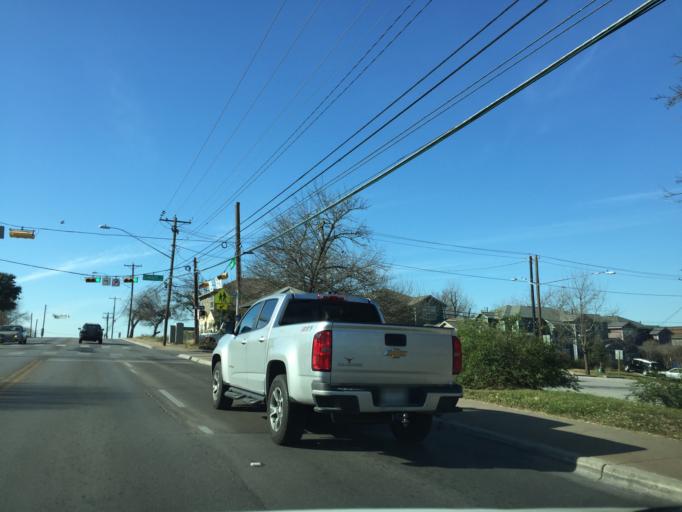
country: US
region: Texas
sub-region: Travis County
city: Austin
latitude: 30.2345
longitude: -97.7433
